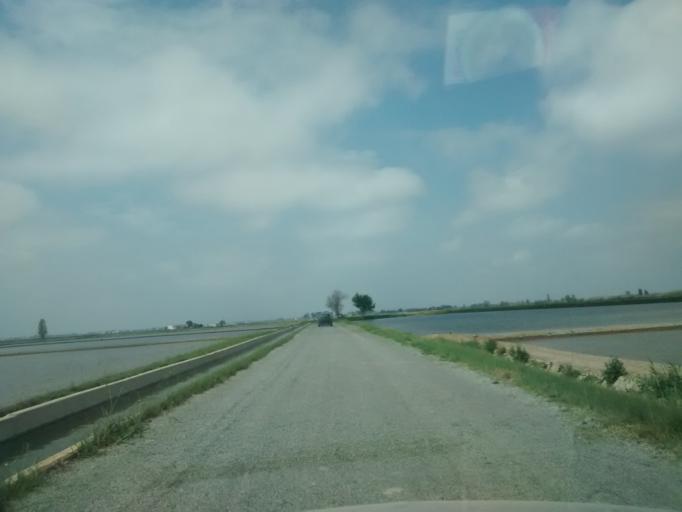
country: ES
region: Catalonia
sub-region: Provincia de Tarragona
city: Deltebre
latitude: 40.6888
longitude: 0.7818
